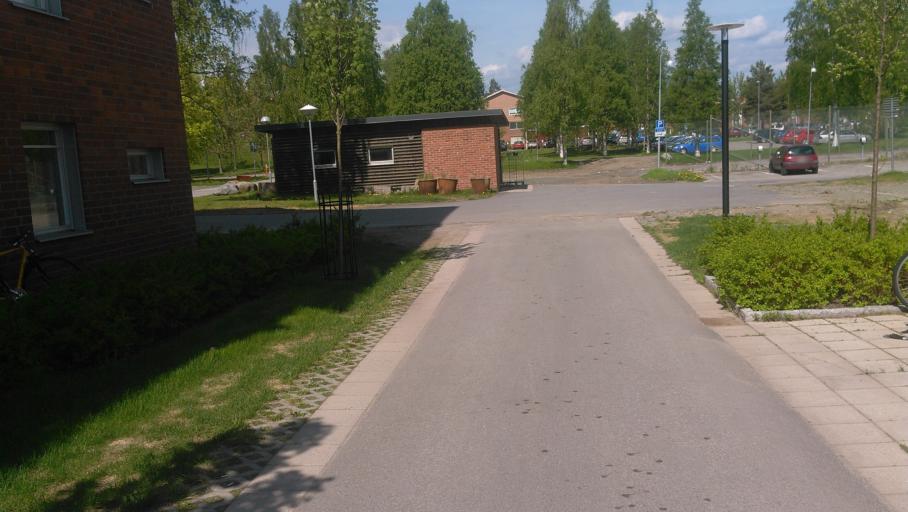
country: SE
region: Vaesterbotten
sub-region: Umea Kommun
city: Umea
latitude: 63.8072
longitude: 20.3093
